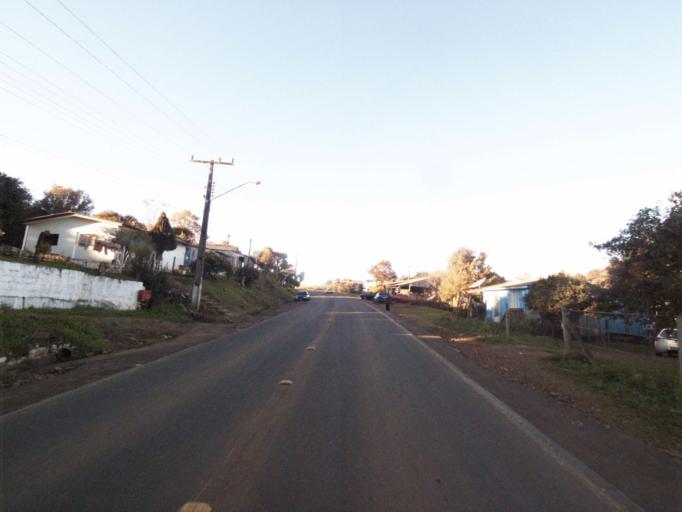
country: AR
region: Misiones
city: Bernardo de Irigoyen
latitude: -26.2612
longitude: -53.6204
